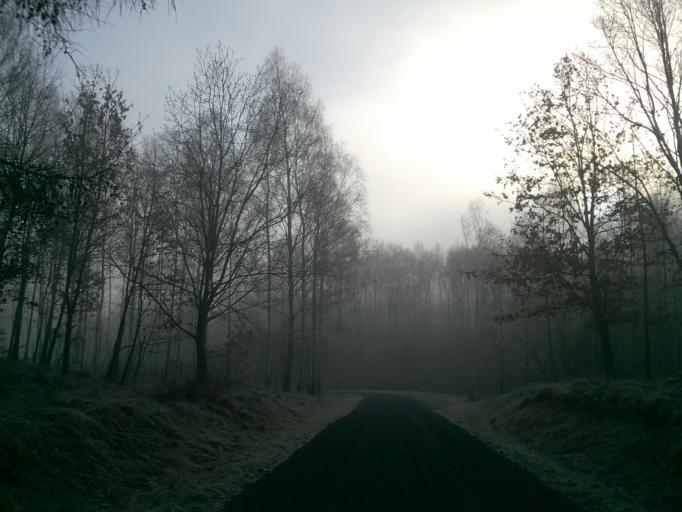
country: PL
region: Kujawsko-Pomorskie
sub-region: Powiat nakielski
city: Kcynia
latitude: 53.0474
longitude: 17.4900
